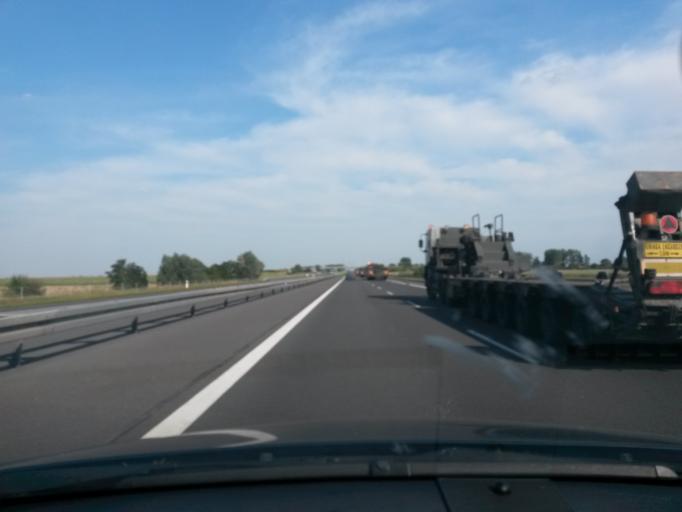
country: PL
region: Greater Poland Voivodeship
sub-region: Powiat wrzesinski
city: Wrzesnia
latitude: 52.2969
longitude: 17.6415
